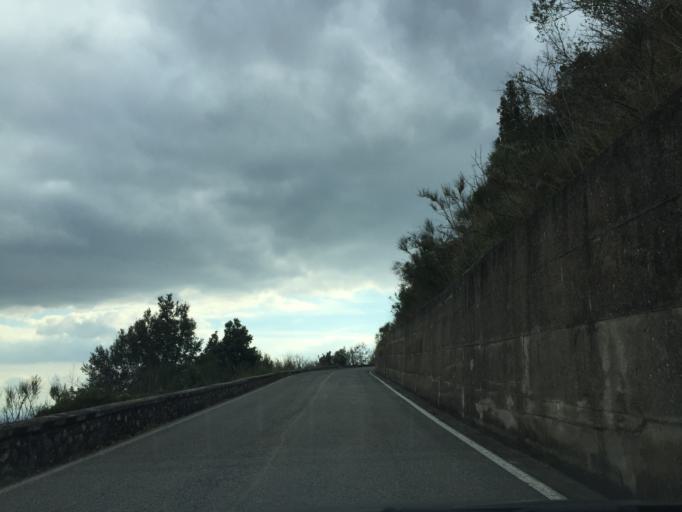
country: IT
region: Latium
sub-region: Provincia di Frosinone
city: Cassino
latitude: 41.4888
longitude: 13.8193
